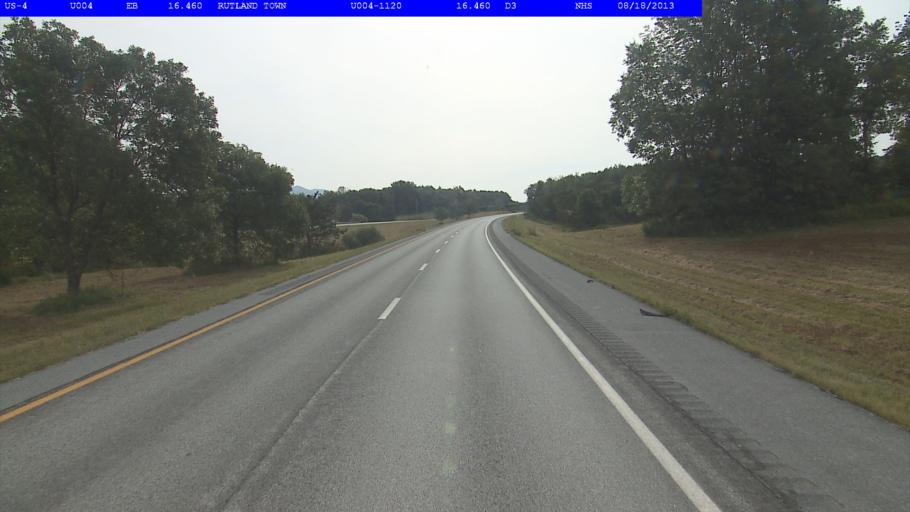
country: US
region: Vermont
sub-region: Rutland County
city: West Rutland
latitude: 43.5923
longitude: -73.0097
